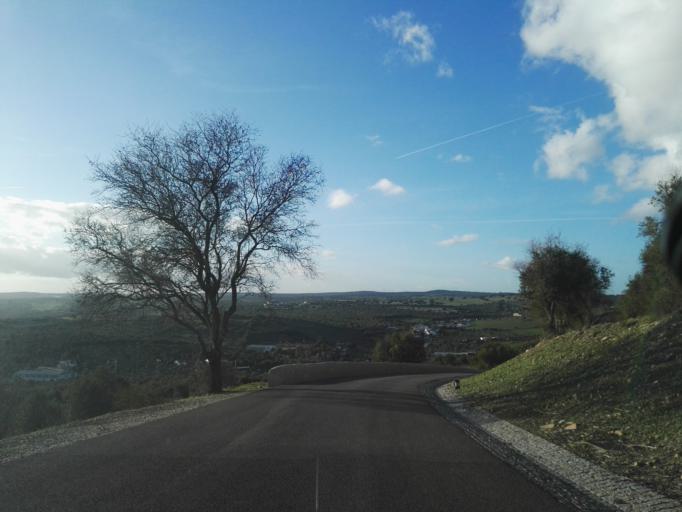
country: PT
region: Portalegre
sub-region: Elvas
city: Elvas
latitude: 38.8927
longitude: -7.1651
